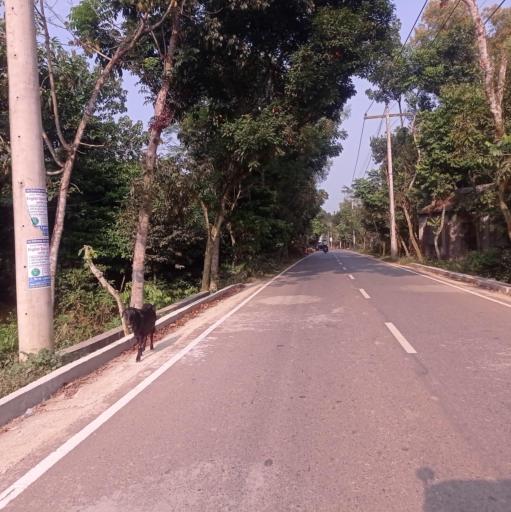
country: BD
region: Dhaka
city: Bhairab Bazar
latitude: 24.0603
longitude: 90.8396
